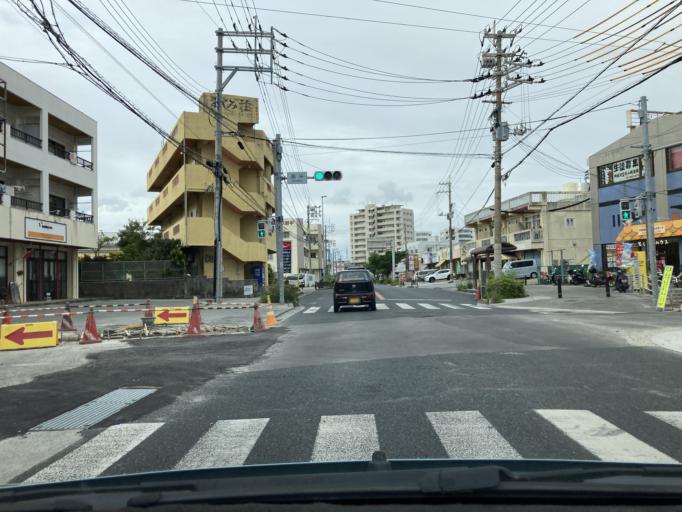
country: JP
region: Okinawa
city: Itoman
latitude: 26.1441
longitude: 127.6729
